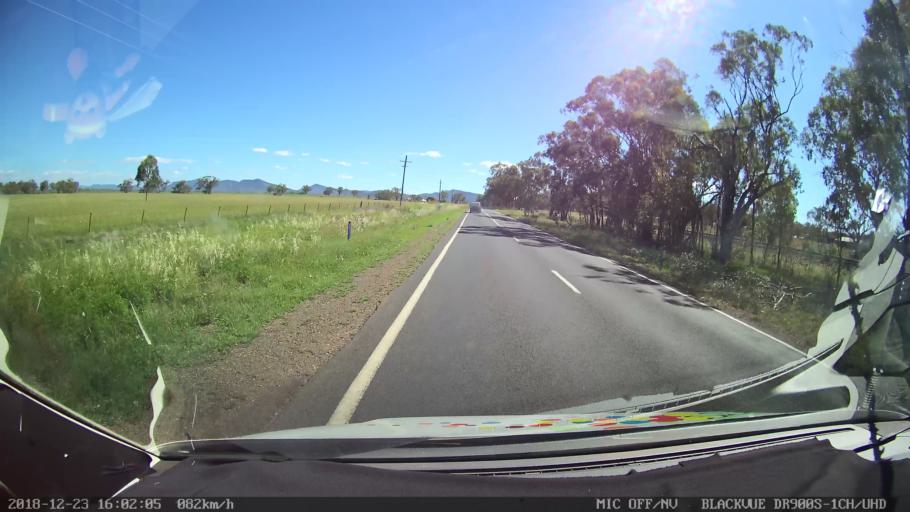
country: AU
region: New South Wales
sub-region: Tamworth Municipality
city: Phillip
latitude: -31.2284
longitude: 150.8119
